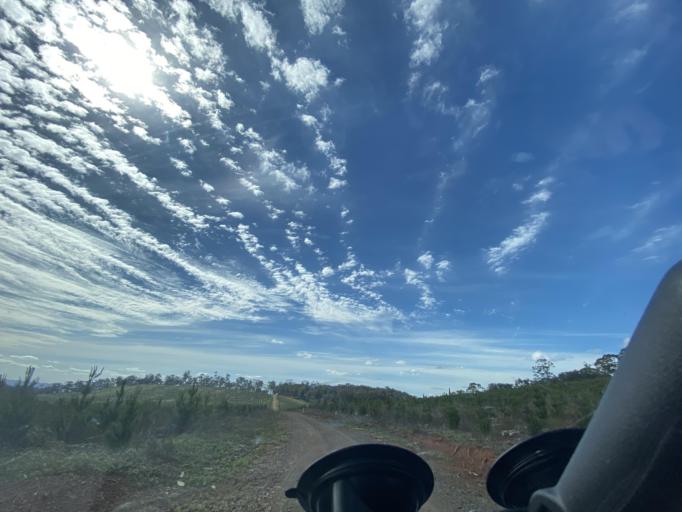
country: AU
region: Victoria
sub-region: Mansfield
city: Mansfield
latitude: -36.8240
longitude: 146.1035
